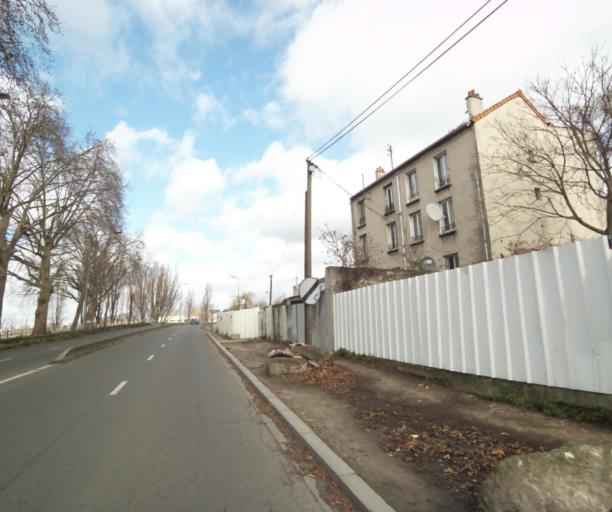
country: FR
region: Ile-de-France
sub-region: Departement de Seine-Saint-Denis
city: Villetaneuse
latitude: 48.9393
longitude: 2.3416
